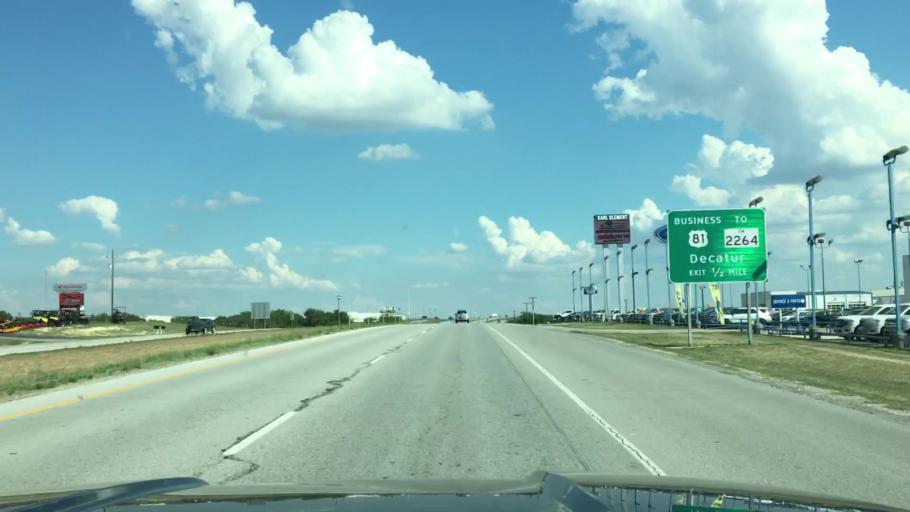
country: US
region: Texas
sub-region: Wise County
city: Decatur
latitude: 33.2113
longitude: -97.5780
